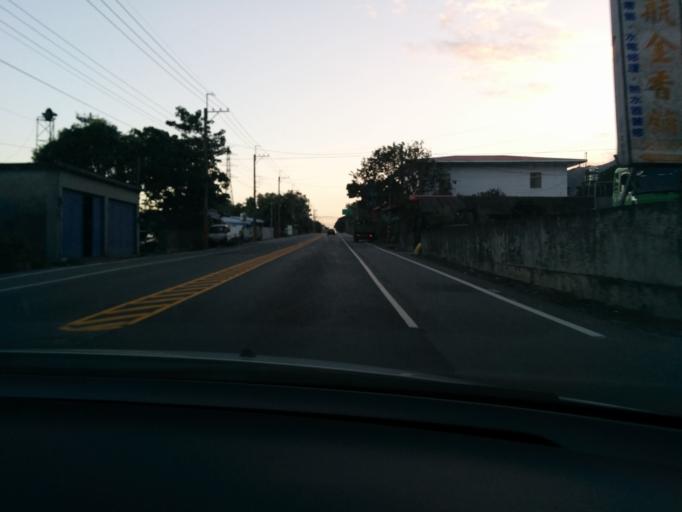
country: TW
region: Taiwan
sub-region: Taitung
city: Taitung
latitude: 22.9784
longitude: 121.1374
